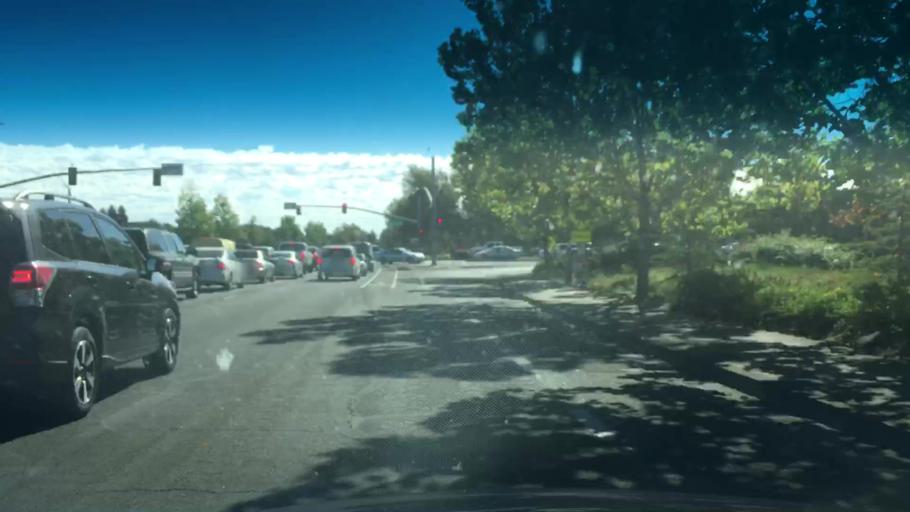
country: US
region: California
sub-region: Sacramento County
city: Laguna
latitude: 38.4561
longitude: -121.4064
